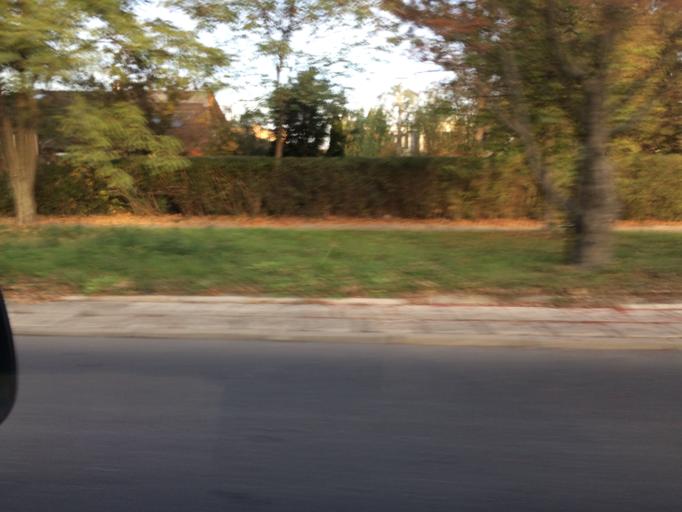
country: PL
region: Opole Voivodeship
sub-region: Powiat opolski
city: Opole
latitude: 50.6729
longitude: 17.9753
